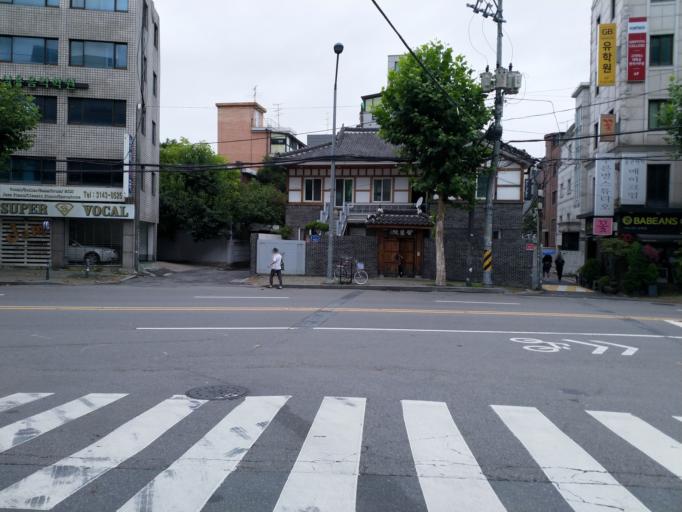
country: KR
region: Seoul
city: Seoul
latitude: 37.5568
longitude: 126.9222
